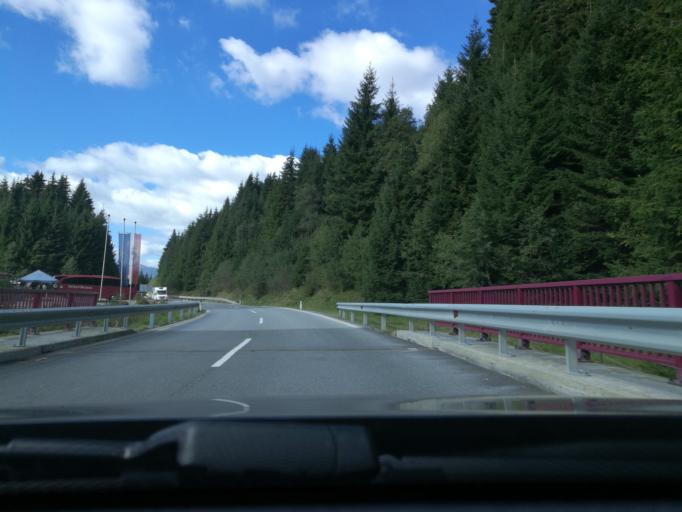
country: AT
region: Salzburg
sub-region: Politischer Bezirk Zell am See
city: Krimml
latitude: 47.2440
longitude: 12.0987
